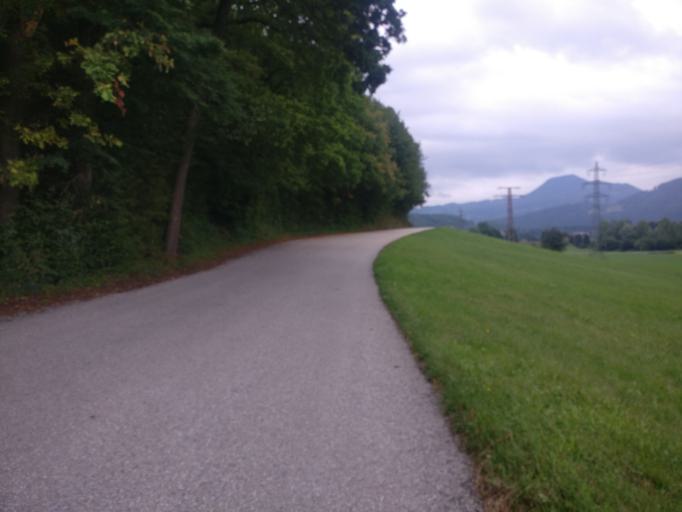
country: AT
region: Styria
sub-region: Politischer Bezirk Graz-Umgebung
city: Frohnleiten
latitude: 47.2573
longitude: 15.3123
